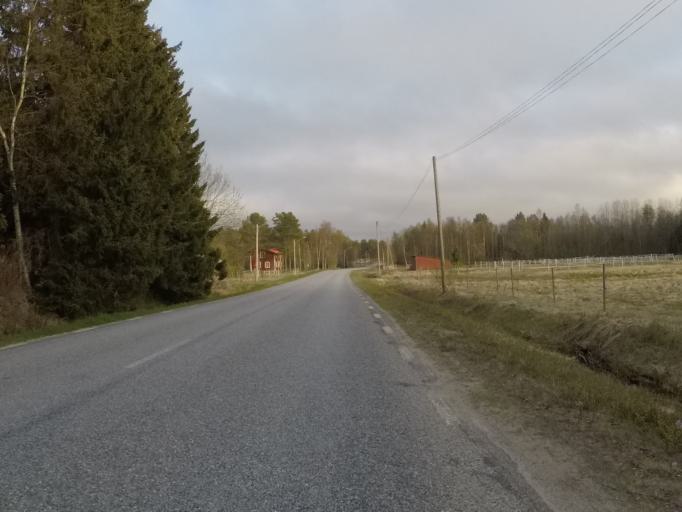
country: SE
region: Vaesterbotten
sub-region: Robertsfors Kommun
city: Robertsfors
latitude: 63.9701
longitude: 20.8119
